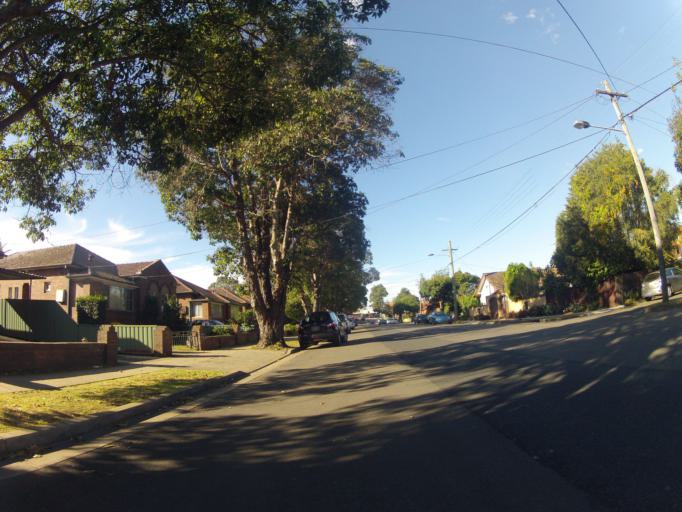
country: AU
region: New South Wales
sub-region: Hurstville
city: Penshurst
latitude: -33.9508
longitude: 151.0794
